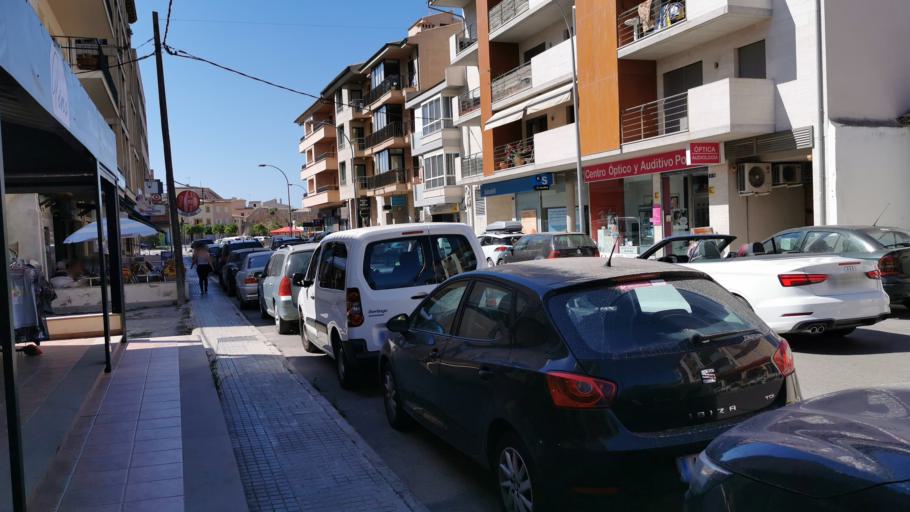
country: ES
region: Balearic Islands
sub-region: Illes Balears
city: Alcudia
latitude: 39.8523
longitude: 3.1248
